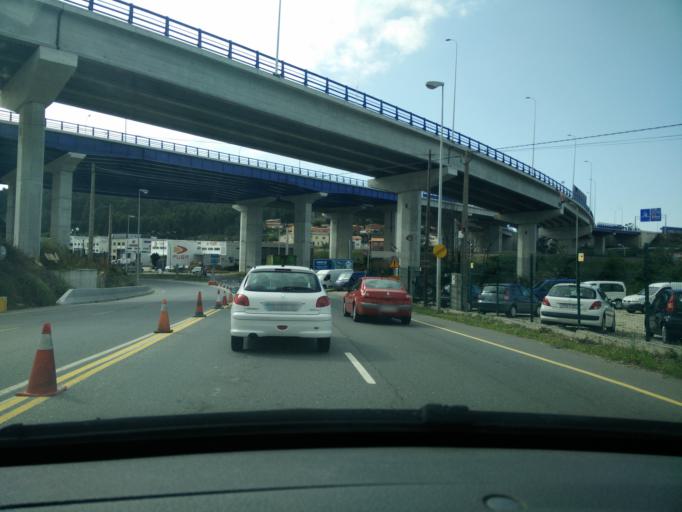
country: ES
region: Galicia
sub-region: Provincia da Coruna
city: A Coruna
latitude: 43.3364
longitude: -8.4201
